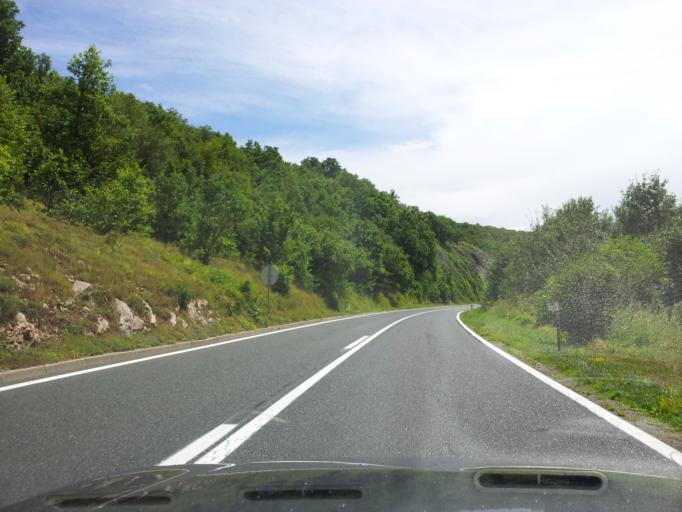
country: BA
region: Federation of Bosnia and Herzegovina
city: Bihac
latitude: 44.6140
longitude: 15.7398
